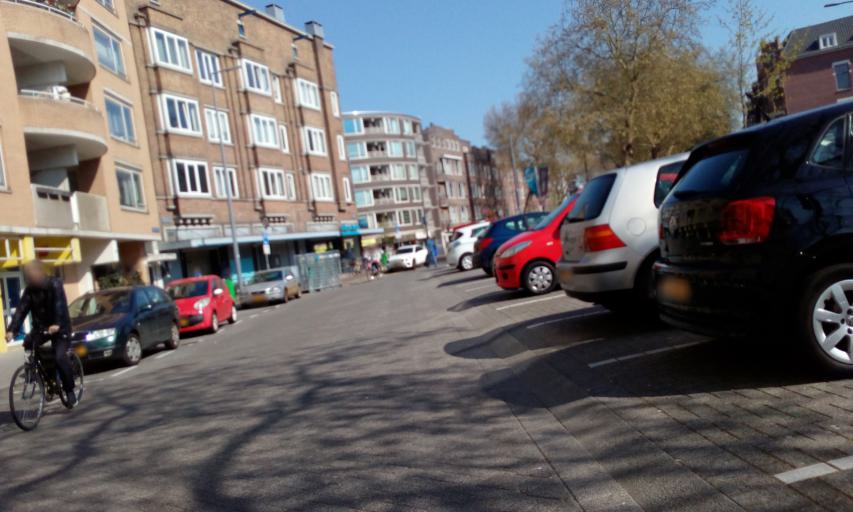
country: NL
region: South Holland
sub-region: Gemeente Rotterdam
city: Rotterdam
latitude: 51.9282
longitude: 4.5016
